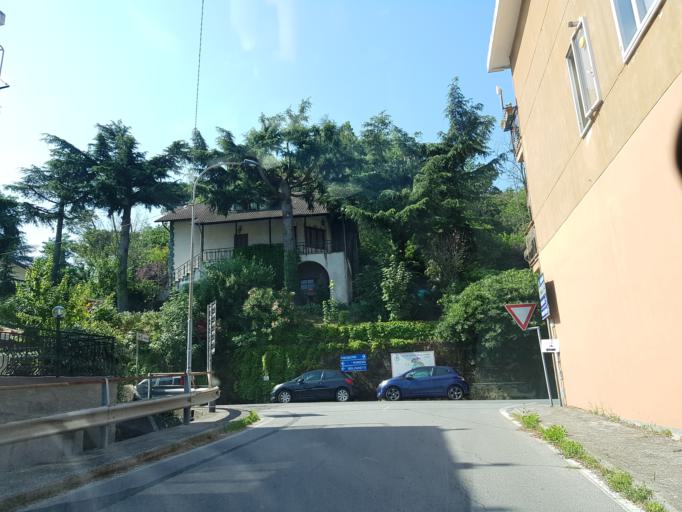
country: IT
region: Liguria
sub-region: Provincia di Genova
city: Pedemonte
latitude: 44.4949
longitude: 8.9132
